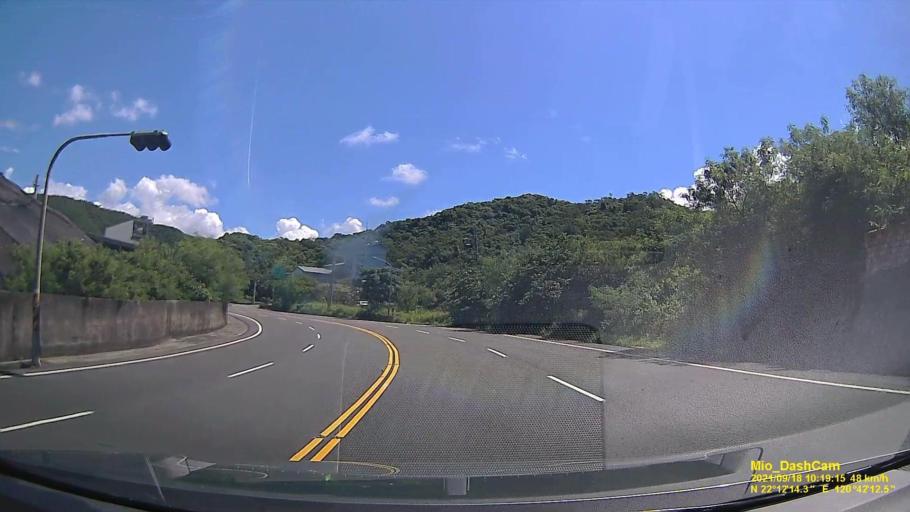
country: TW
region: Taiwan
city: Hengchun
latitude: 22.2040
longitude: 120.7036
